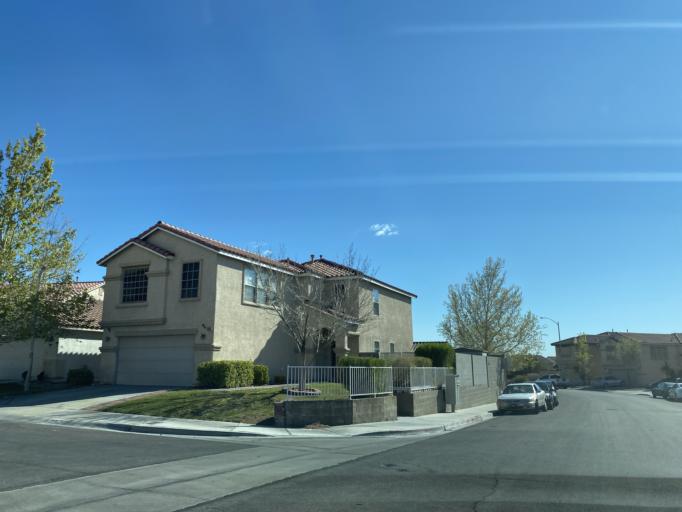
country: US
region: Nevada
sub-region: Clark County
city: Summerlin South
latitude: 36.3031
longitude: -115.2865
